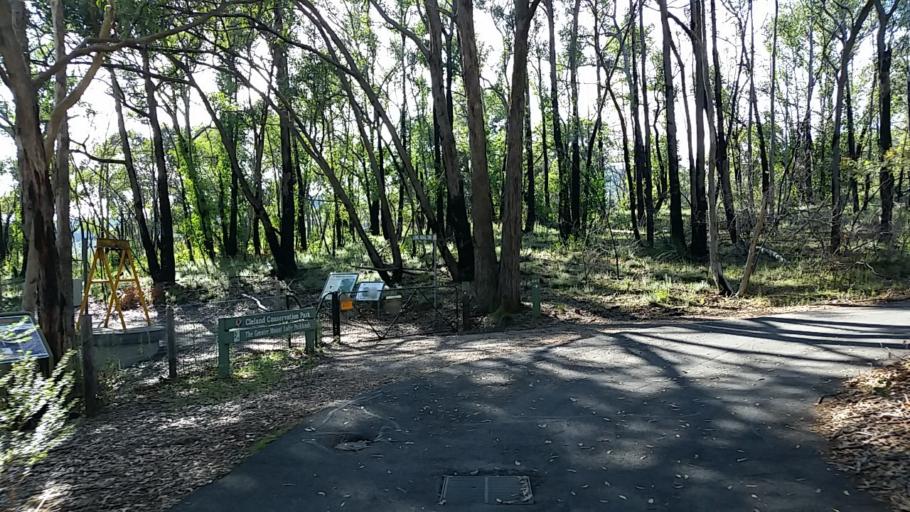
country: AU
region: South Australia
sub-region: Adelaide Hills
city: Crafers
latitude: -34.9651
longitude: 138.6984
